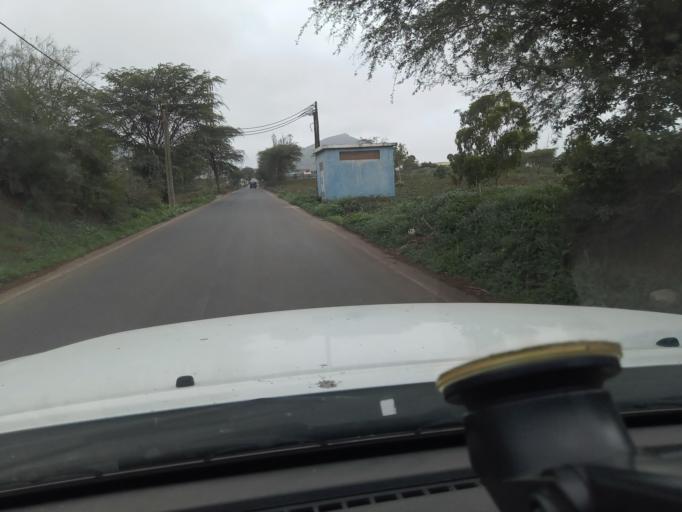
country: CV
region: Santa Catarina
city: Assomada
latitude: 15.1292
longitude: -23.6718
